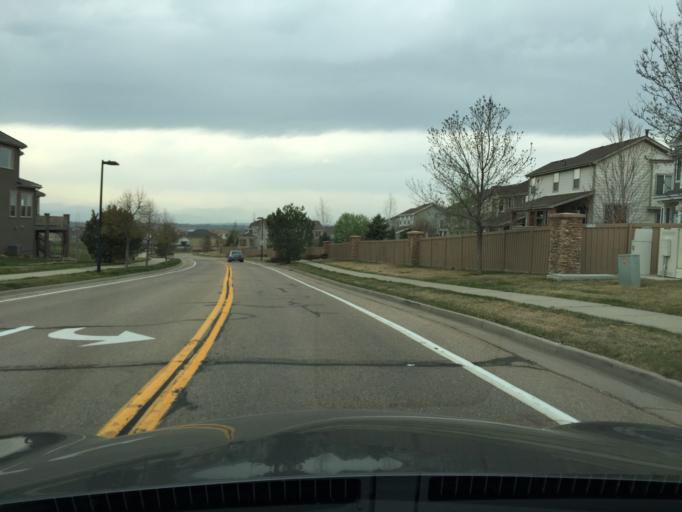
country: US
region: Colorado
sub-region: Boulder County
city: Erie
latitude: 40.0078
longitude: -105.0187
